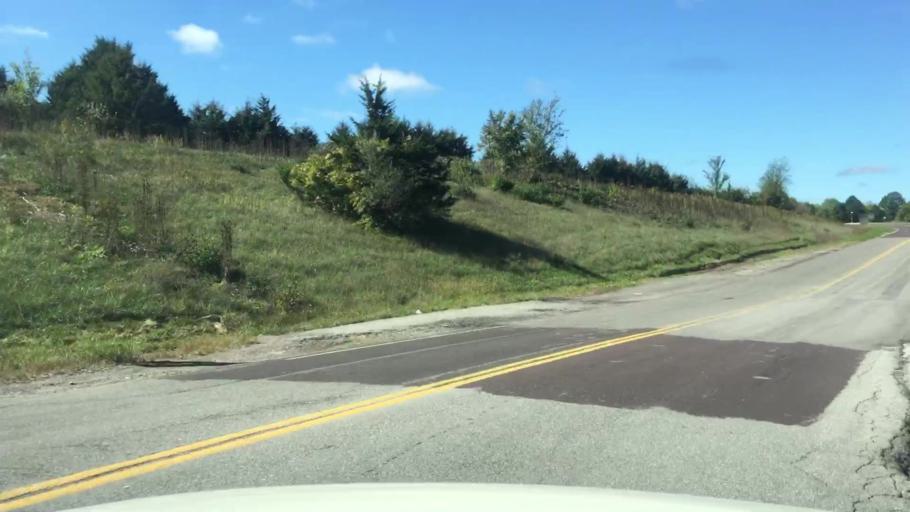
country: US
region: Missouri
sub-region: Boone County
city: Ashland
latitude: 38.7308
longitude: -92.2545
